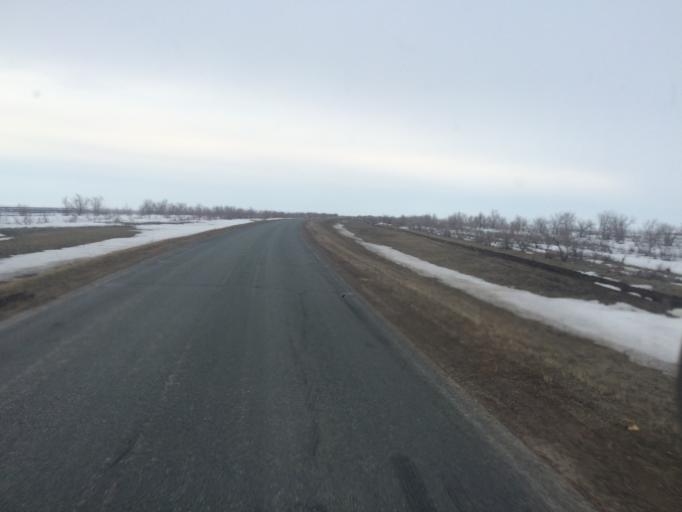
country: KZ
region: Batys Qazaqstan
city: Oral
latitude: 51.4339
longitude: 51.2648
